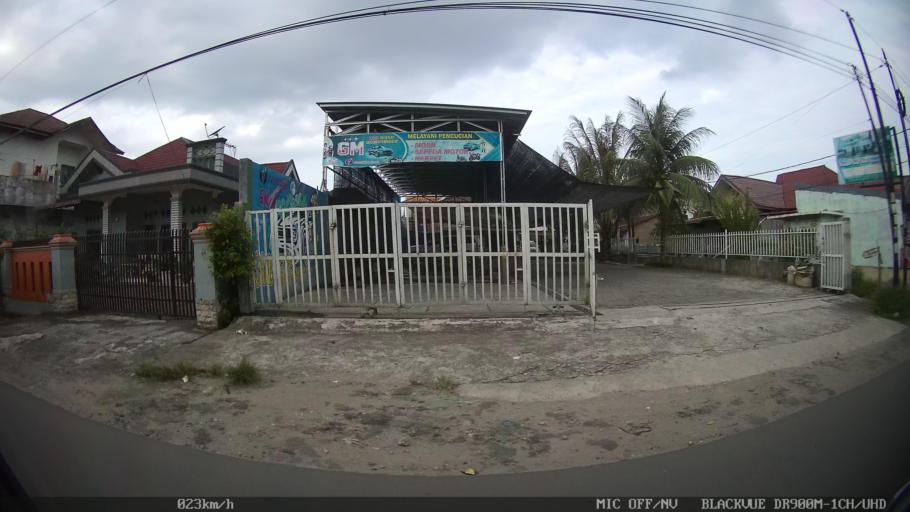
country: ID
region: North Sumatra
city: Sunggal
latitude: 3.5217
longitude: 98.6177
